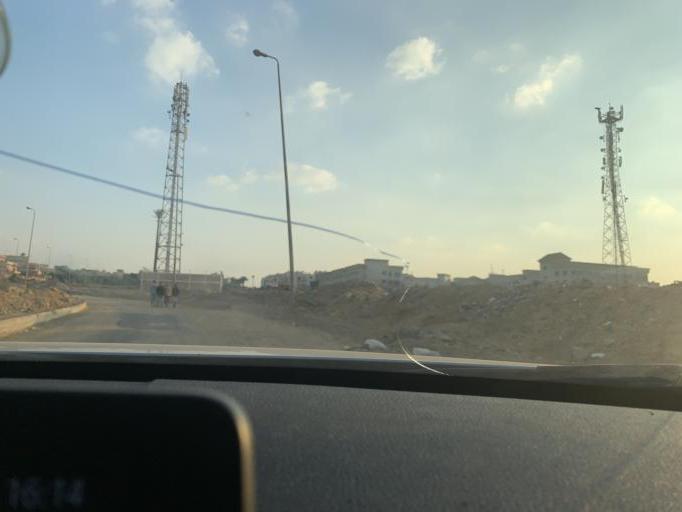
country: EG
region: Muhafazat al Qalyubiyah
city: Al Khankah
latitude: 30.0219
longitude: 31.4813
